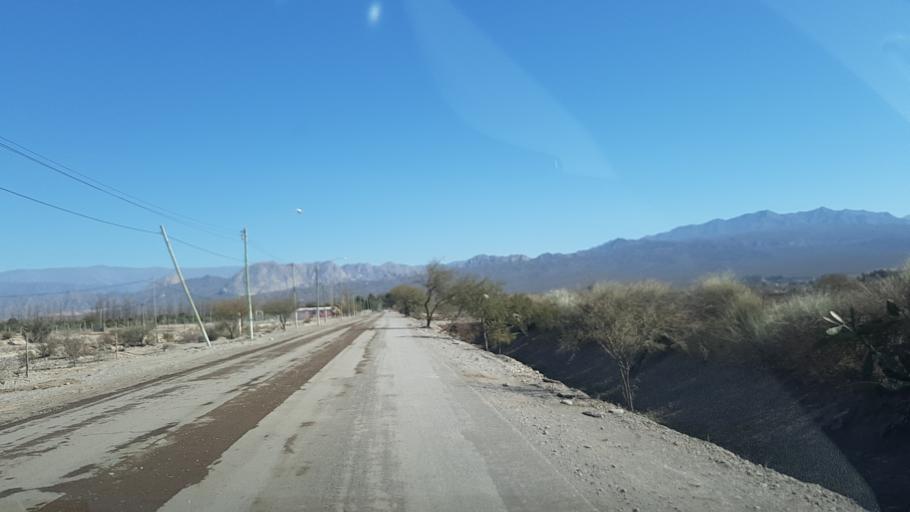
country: AR
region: San Juan
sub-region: Departamento de Zonda
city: Zonda
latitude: -31.4692
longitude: -68.7249
